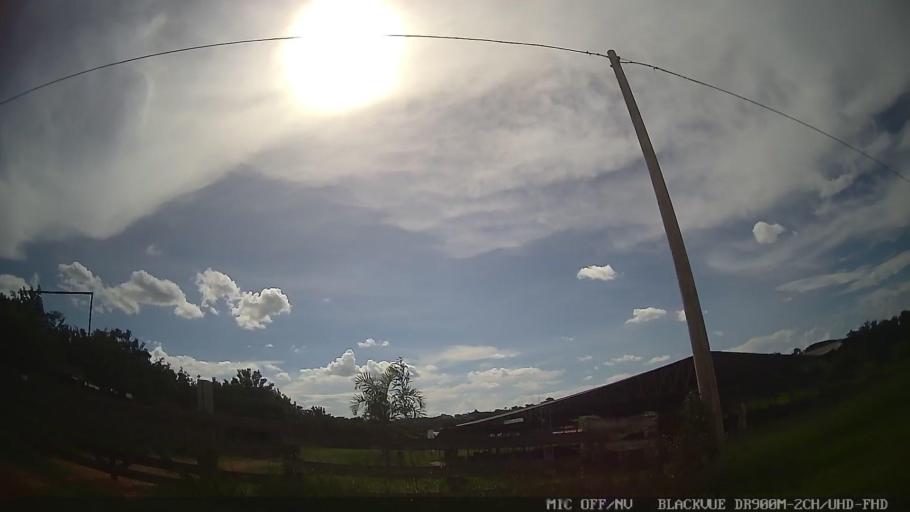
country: BR
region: Sao Paulo
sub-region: Conchas
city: Conchas
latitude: -23.0300
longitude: -47.9955
